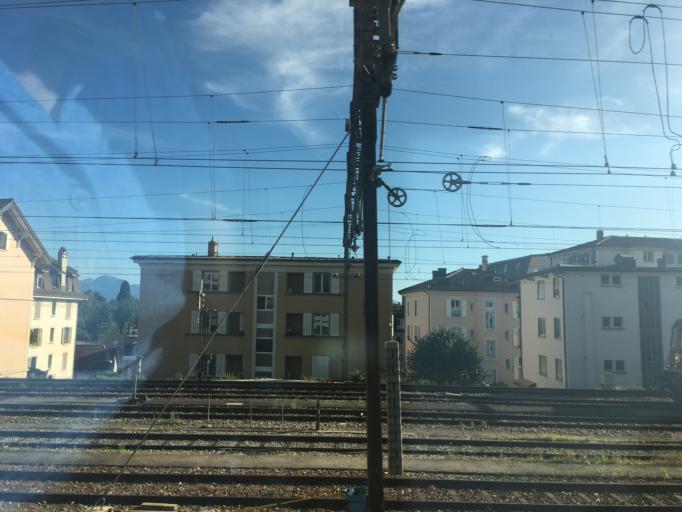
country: CH
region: Vaud
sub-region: Lausanne District
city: Lausanne
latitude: 46.5178
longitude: 6.6233
